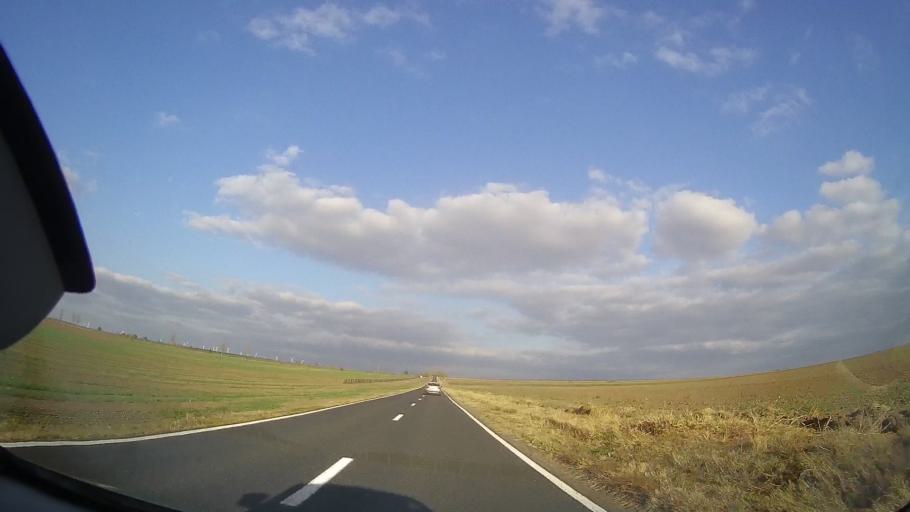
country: RO
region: Tulcea
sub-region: Comuna Topolog
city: Topolog
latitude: 44.8432
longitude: 28.3095
